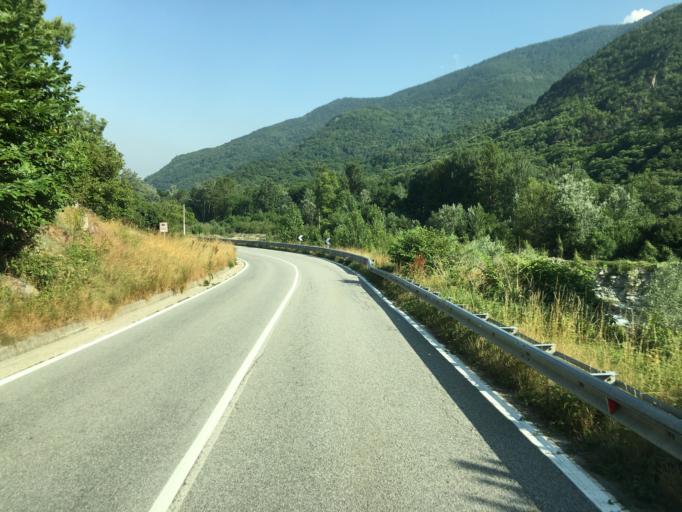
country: IT
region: Piedmont
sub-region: Provincia di Torino
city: Roure
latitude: 44.9836
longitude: 7.1470
